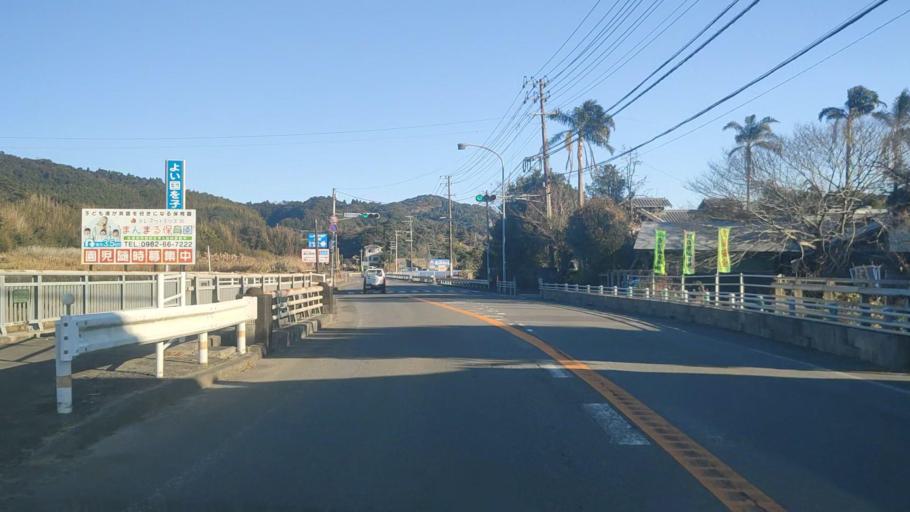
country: JP
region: Miyazaki
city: Nobeoka
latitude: 32.3619
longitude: 131.6228
